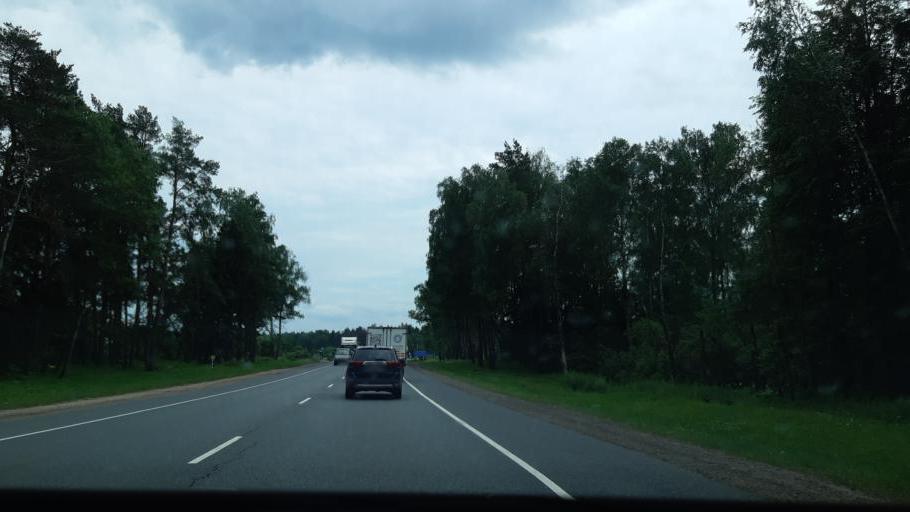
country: RU
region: Moskovskaya
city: Dorokhovo
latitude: 55.4932
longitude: 36.3516
